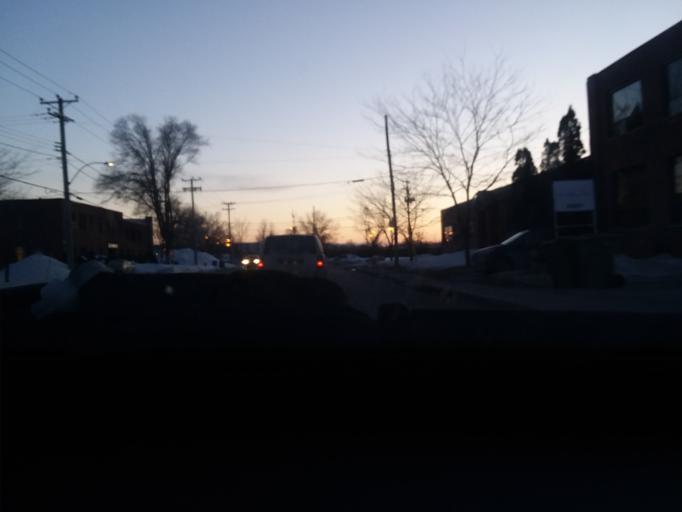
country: CA
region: Quebec
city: Montreal-Ouest
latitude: 45.4371
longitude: -73.6436
